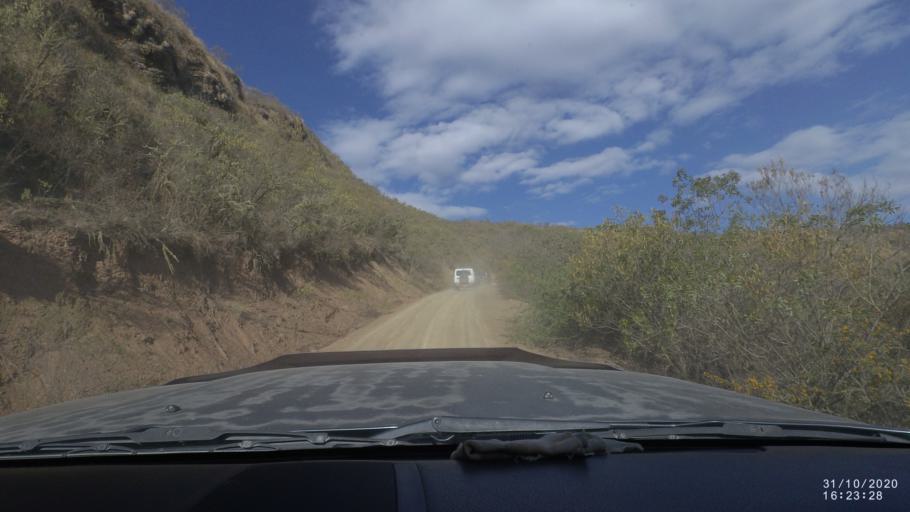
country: BO
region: Chuquisaca
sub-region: Provincia Zudanez
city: Mojocoya
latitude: -18.3990
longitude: -64.5905
